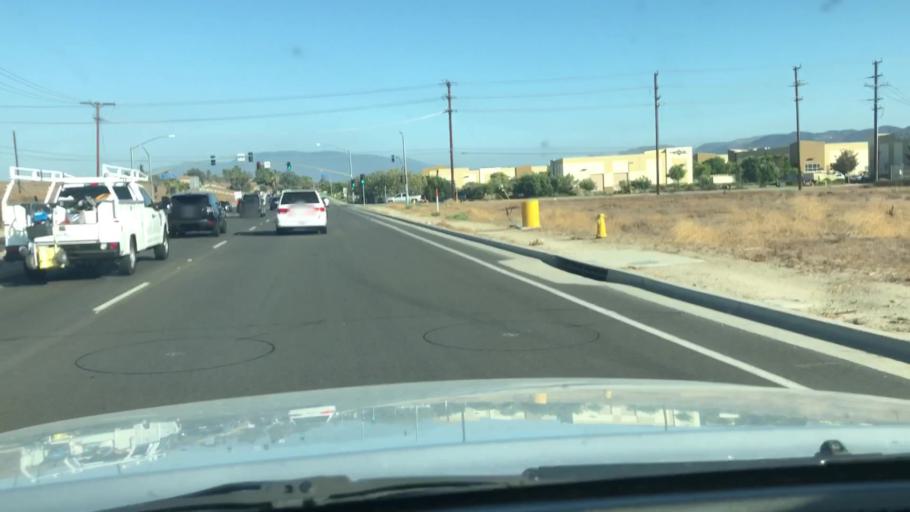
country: US
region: California
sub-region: Riverside County
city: Murrieta
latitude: 33.5410
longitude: -117.1877
